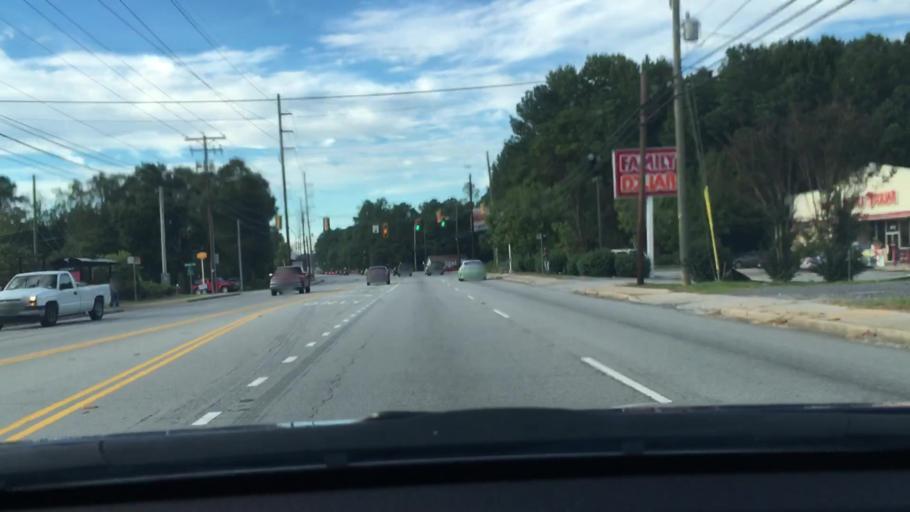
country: US
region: South Carolina
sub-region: Lexington County
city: Saint Andrews
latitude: 34.0561
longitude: -81.1106
